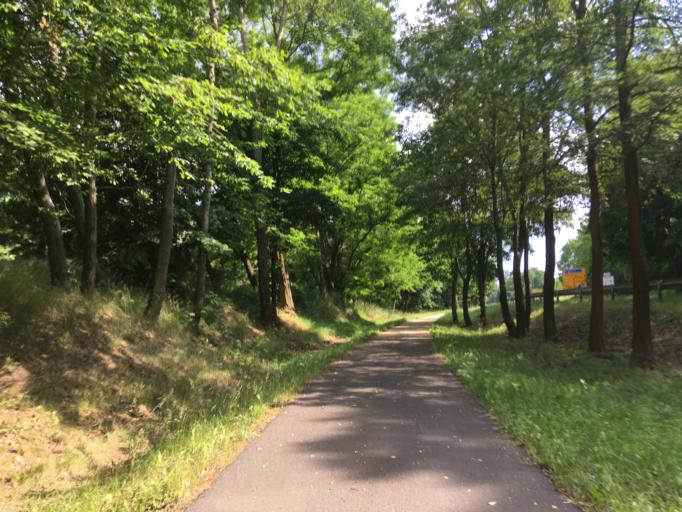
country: DE
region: Brandenburg
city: Furstenwalde
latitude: 52.3838
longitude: 14.0864
